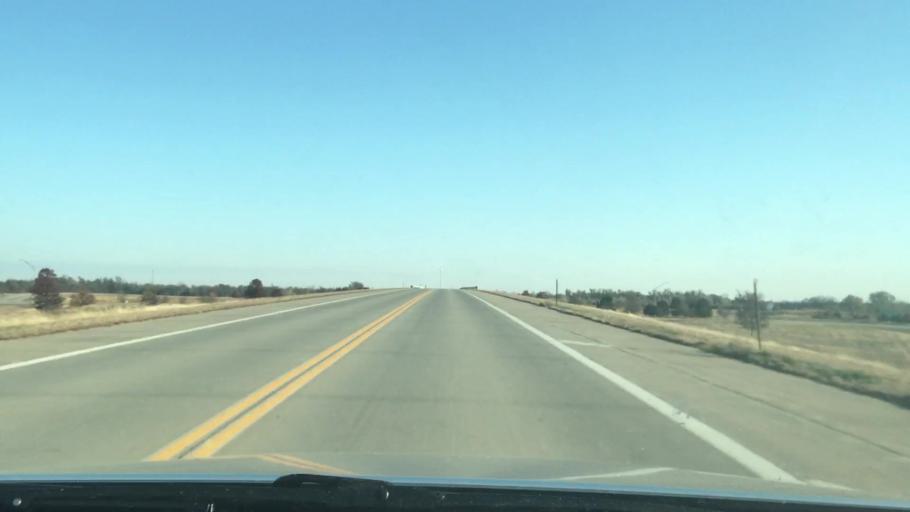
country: US
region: Kansas
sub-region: Reno County
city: Hutchinson
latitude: 38.0933
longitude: -97.9997
